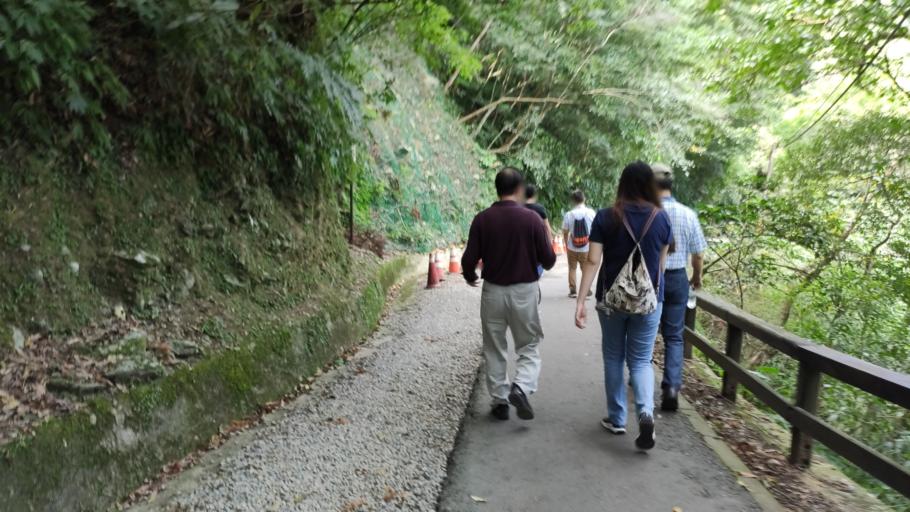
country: TW
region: Taiwan
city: Daxi
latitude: 24.8287
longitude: 121.4452
